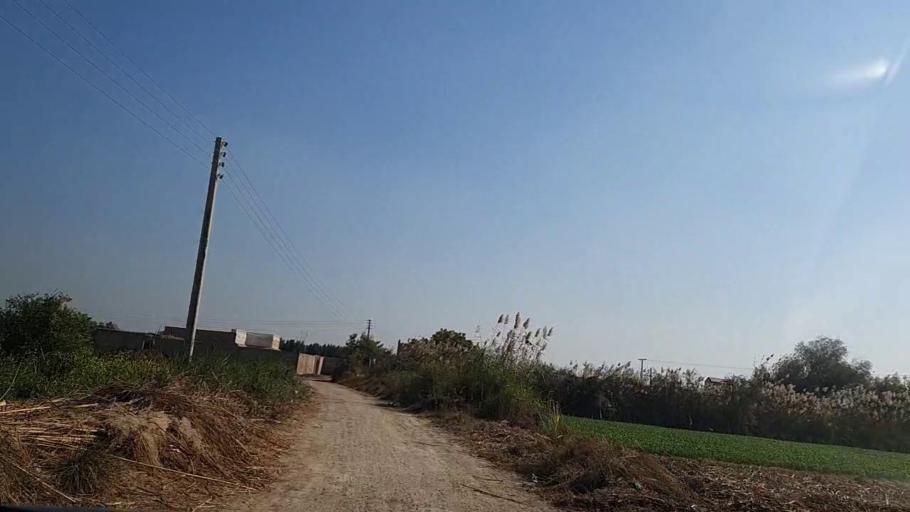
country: PK
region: Sindh
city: Sakrand
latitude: 26.2290
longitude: 68.3118
